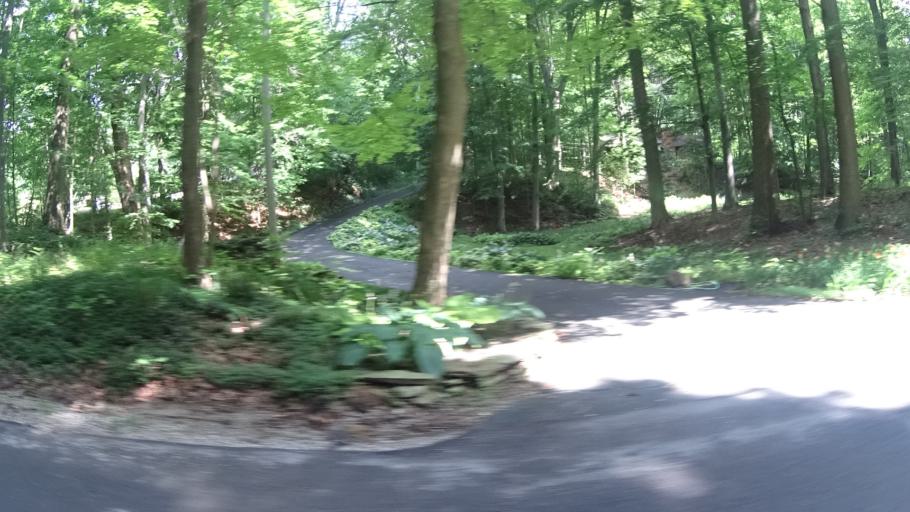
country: US
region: Ohio
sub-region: Huron County
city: Wakeman
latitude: 41.3192
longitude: -82.3732
